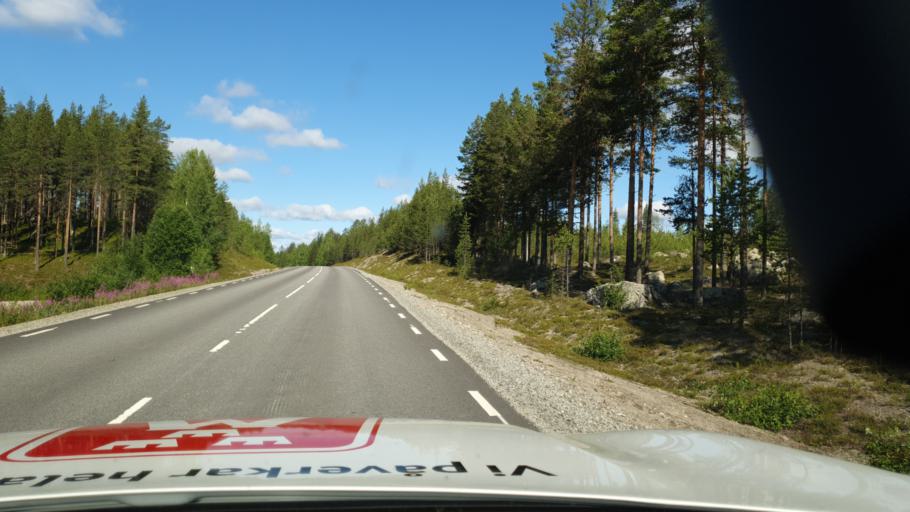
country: SE
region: Vaesterbotten
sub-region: Norsjo Kommun
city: Norsjoe
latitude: 64.6830
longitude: 19.2389
